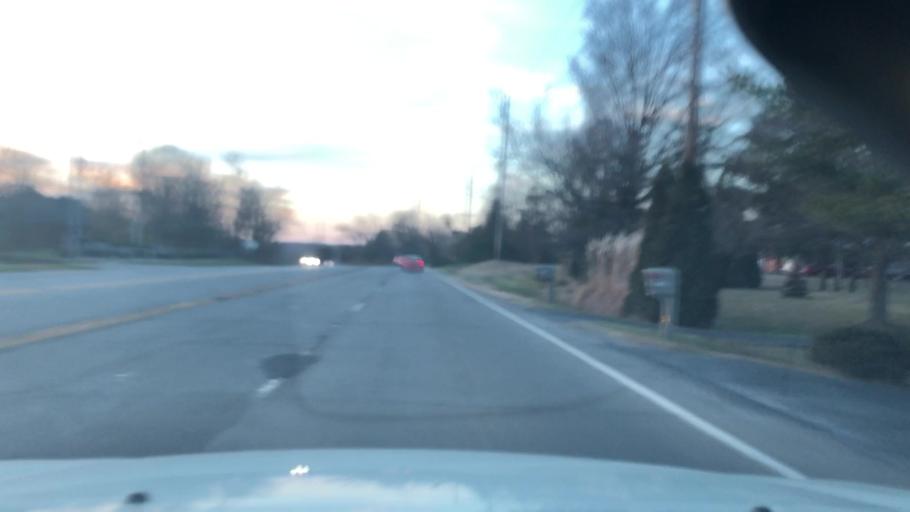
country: US
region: Kentucky
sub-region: Jefferson County
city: Anchorage
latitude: 38.2358
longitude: -85.4605
